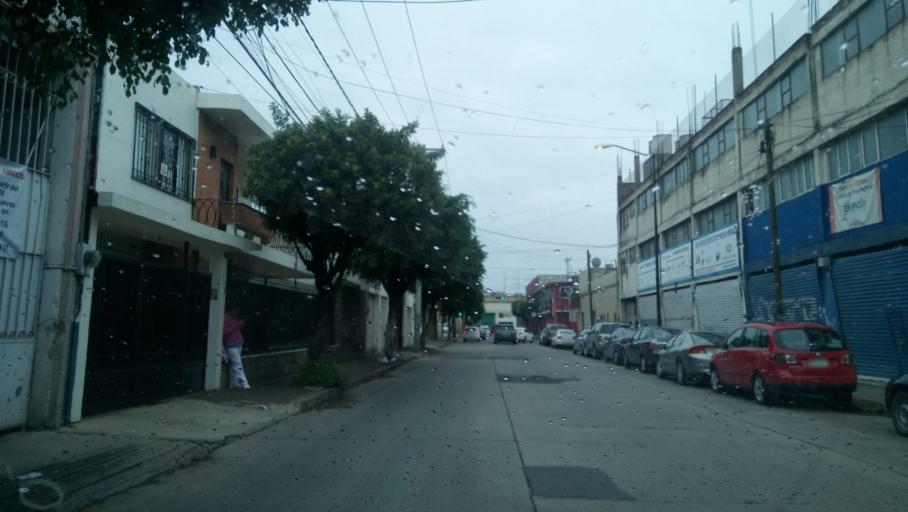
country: MX
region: Guanajuato
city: Leon
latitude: 21.1184
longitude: -101.6740
